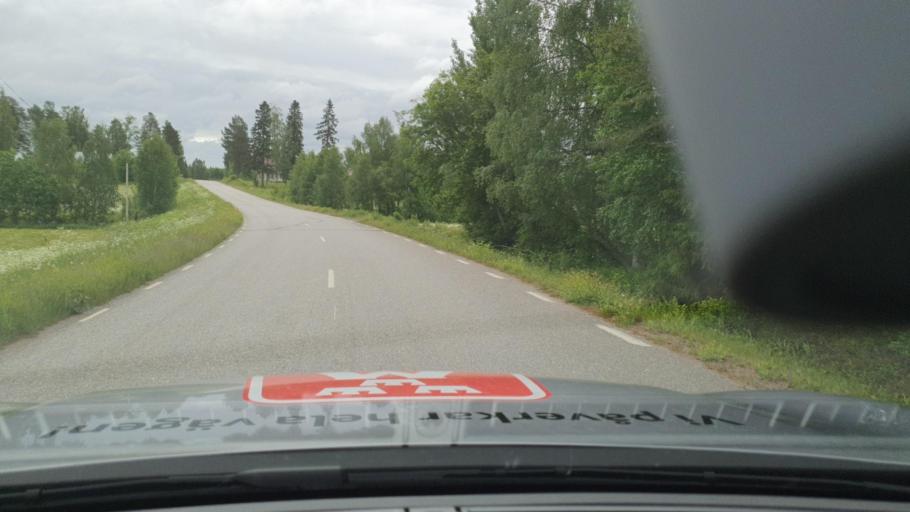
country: SE
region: Norrbotten
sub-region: Lulea Kommun
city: Ranea
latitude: 65.9312
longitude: 22.1395
